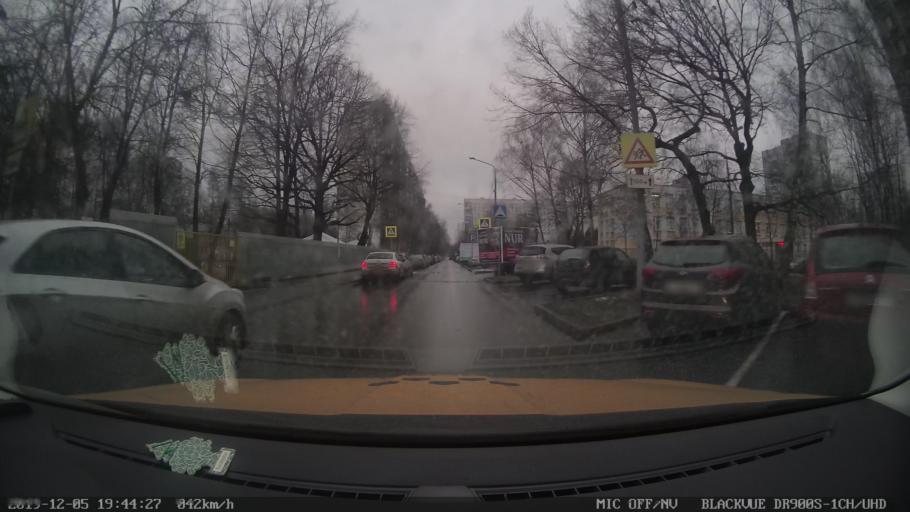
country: RU
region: Moscow
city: Lianozovo
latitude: 55.8999
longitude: 37.5770
